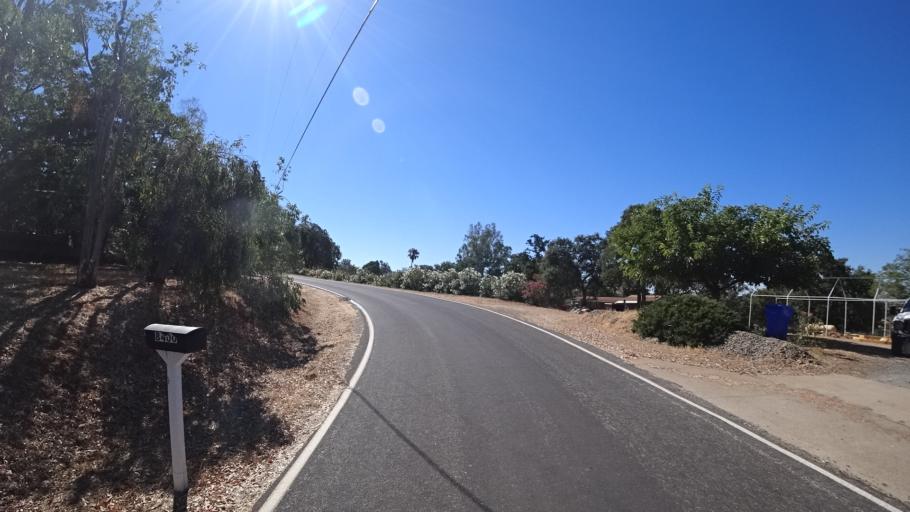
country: US
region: California
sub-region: Calaveras County
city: Rancho Calaveras
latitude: 38.1008
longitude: -120.8650
